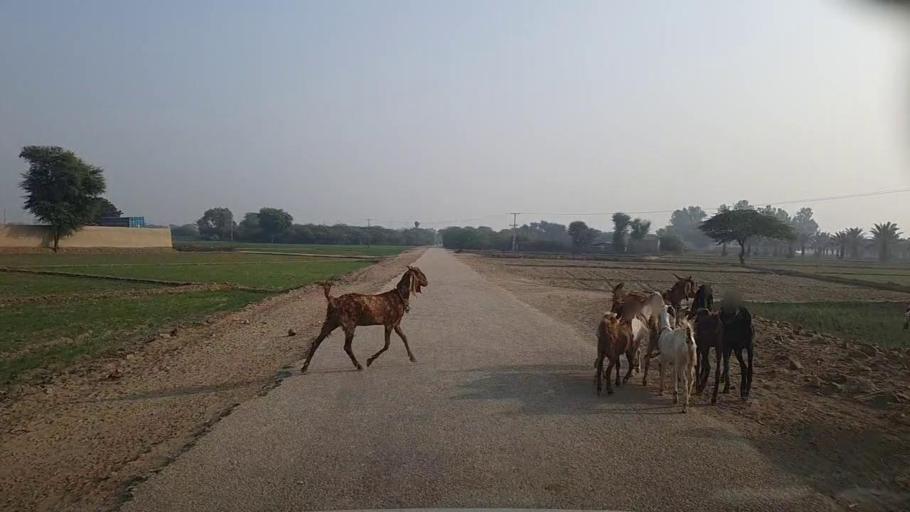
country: PK
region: Sindh
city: Kandiari
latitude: 27.0405
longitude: 68.4780
